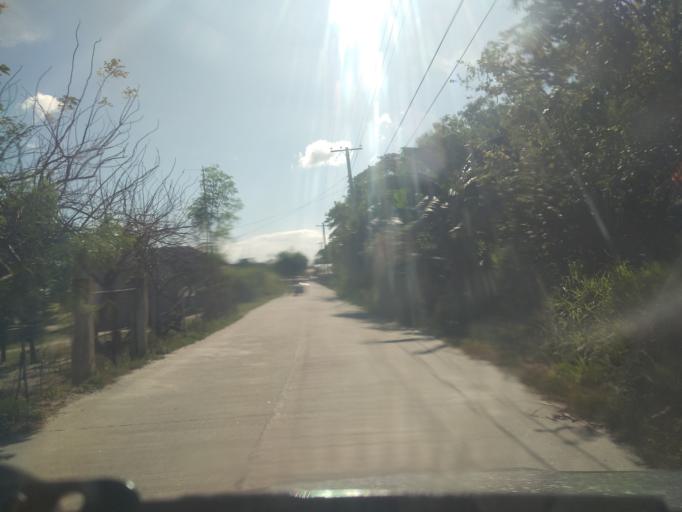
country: PH
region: Central Luzon
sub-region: Province of Pampanga
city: Calibutbut
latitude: 15.0884
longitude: 120.6009
